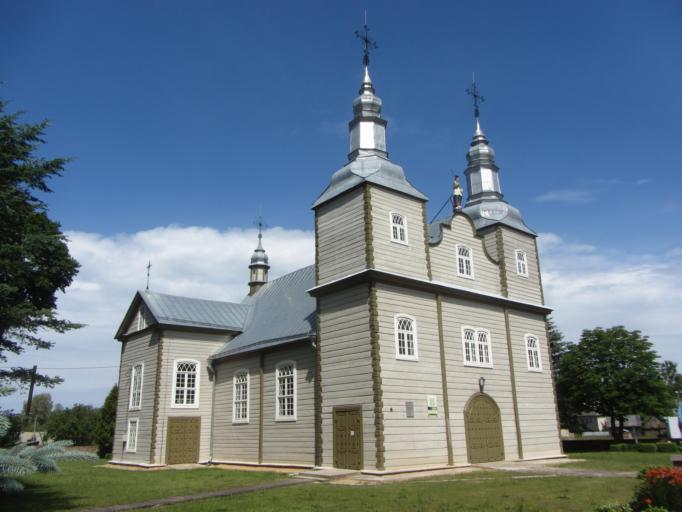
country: LV
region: Nereta
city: Nereta
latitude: 56.1491
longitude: 25.1389
